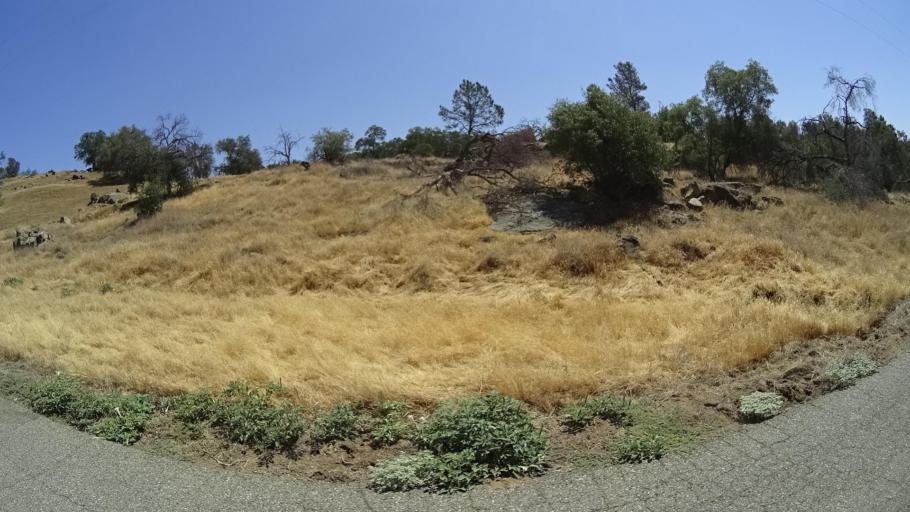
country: US
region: California
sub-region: Mariposa County
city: Mariposa
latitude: 37.2910
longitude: -119.9774
